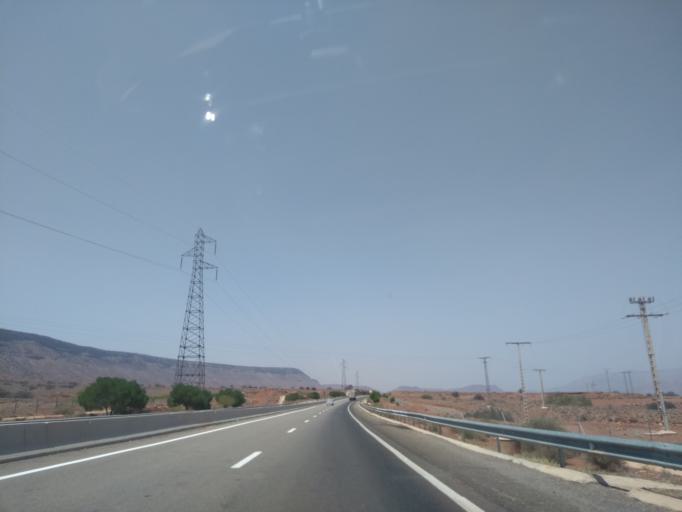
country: MA
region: Marrakech-Tensift-Al Haouz
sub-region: Chichaoua
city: Timezgadiouine
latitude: 30.8884
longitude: -9.0779
